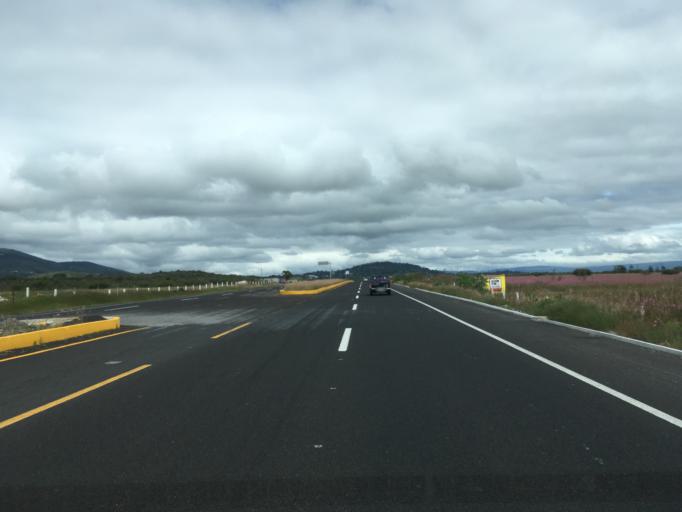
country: MX
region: Hidalgo
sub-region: Atotonilco el Grande
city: Santa Maria Amajac
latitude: 20.3688
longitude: -98.7207
